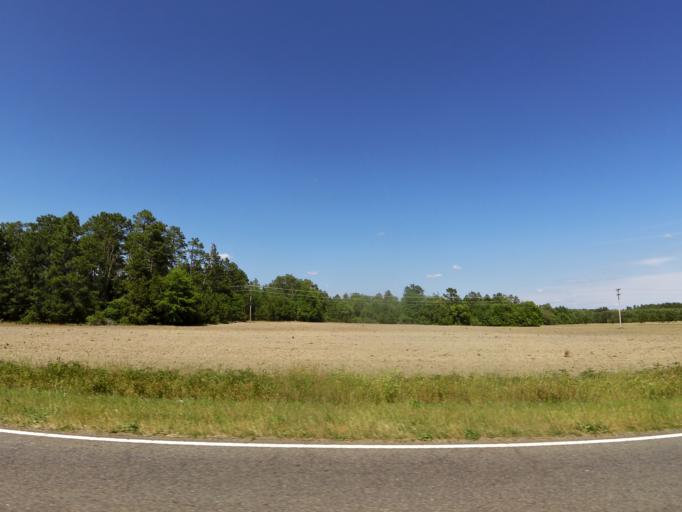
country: US
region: South Carolina
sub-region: Barnwell County
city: Williston
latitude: 33.4894
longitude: -81.5219
